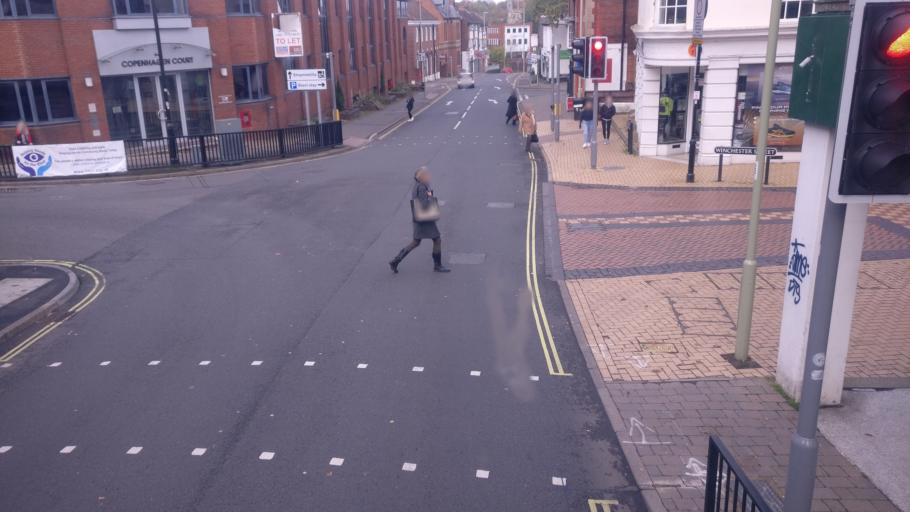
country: GB
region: England
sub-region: Hampshire
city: Basingstoke
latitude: 51.2622
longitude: -1.0888
